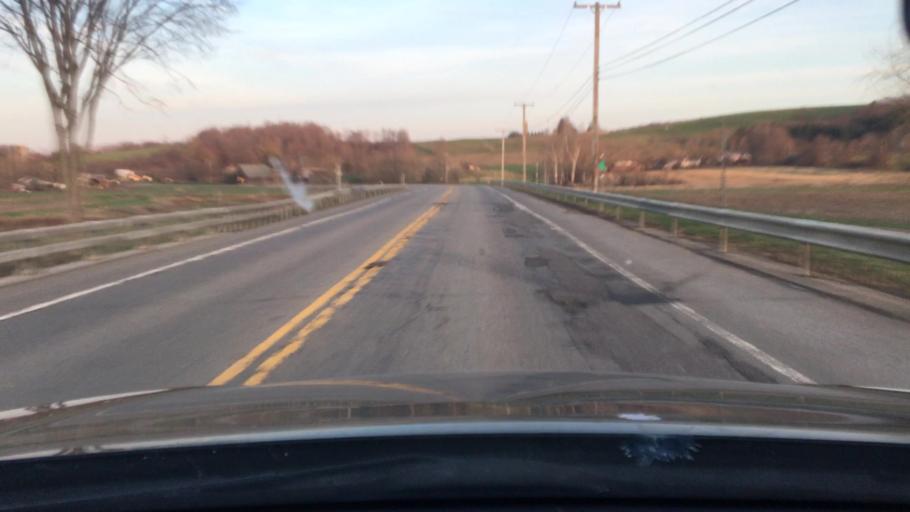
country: US
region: New York
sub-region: Cattaraugus County
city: Randolph
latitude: 42.1946
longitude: -78.9073
